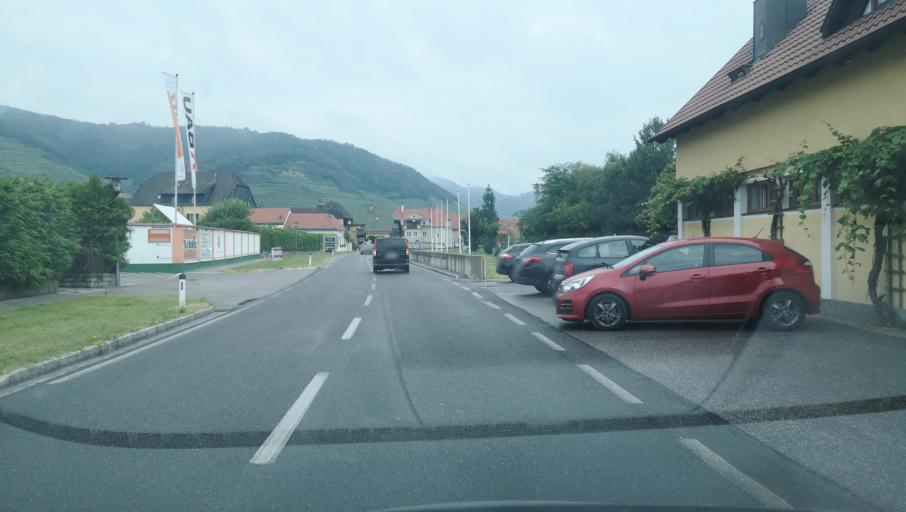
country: AT
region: Lower Austria
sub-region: Politischer Bezirk Krems
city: Weinzierl am Walde
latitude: 48.3930
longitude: 15.4684
